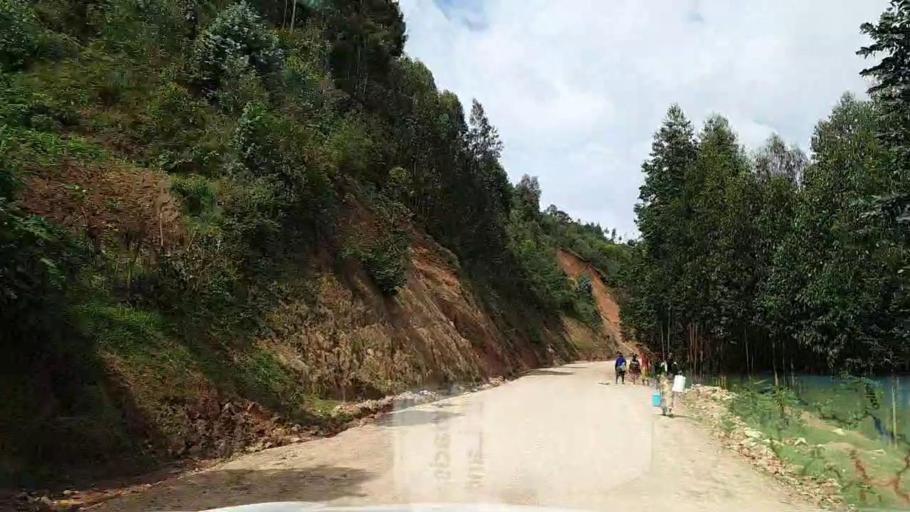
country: RW
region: Southern Province
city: Nzega
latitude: -2.3358
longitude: 29.4413
